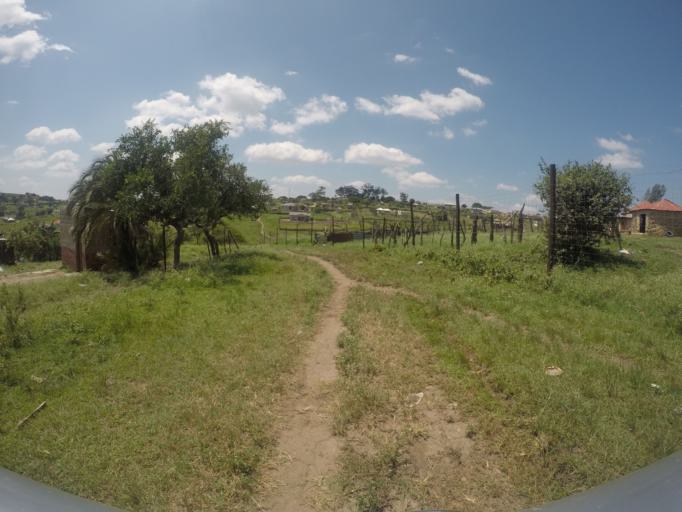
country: ZA
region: KwaZulu-Natal
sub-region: uThungulu District Municipality
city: Empangeni
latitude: -28.6055
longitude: 31.7381
